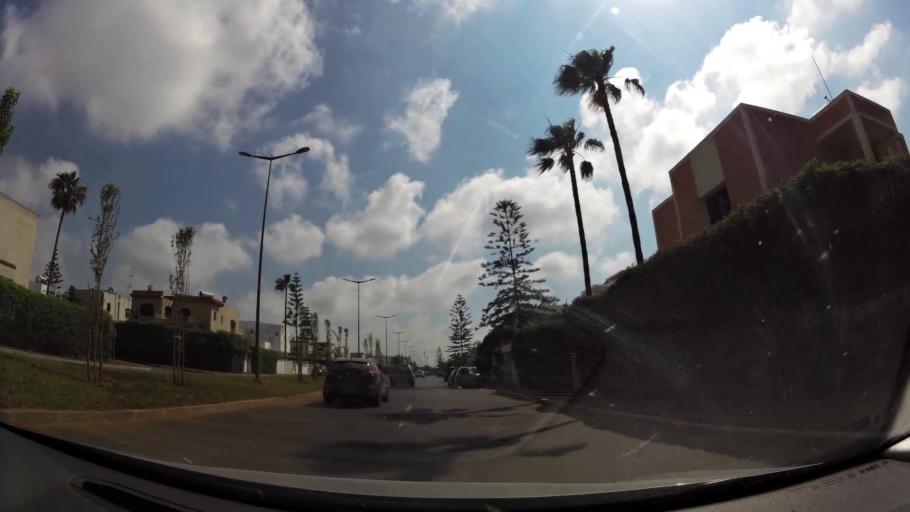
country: MA
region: Rabat-Sale-Zemmour-Zaer
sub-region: Skhirate-Temara
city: Temara
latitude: 33.9639
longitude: -6.8699
